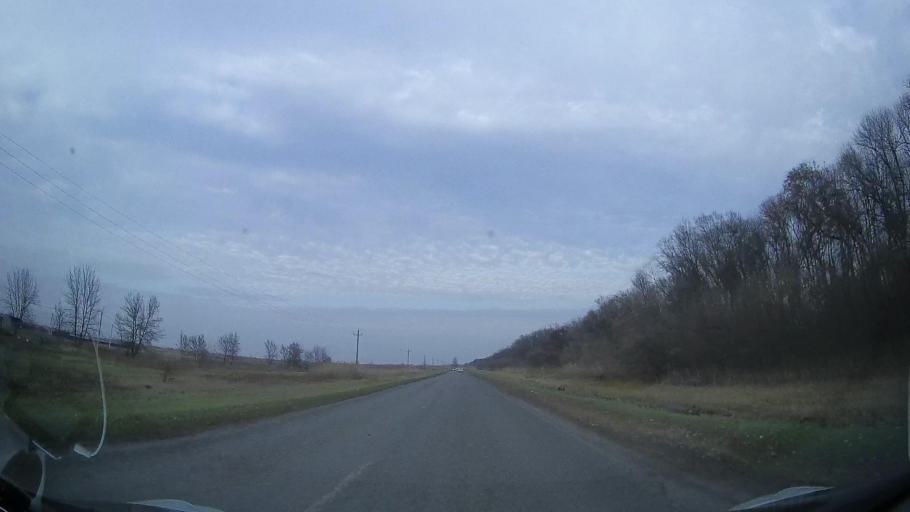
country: RU
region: Rostov
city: Ol'ginskaya
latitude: 47.1375
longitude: 39.8956
